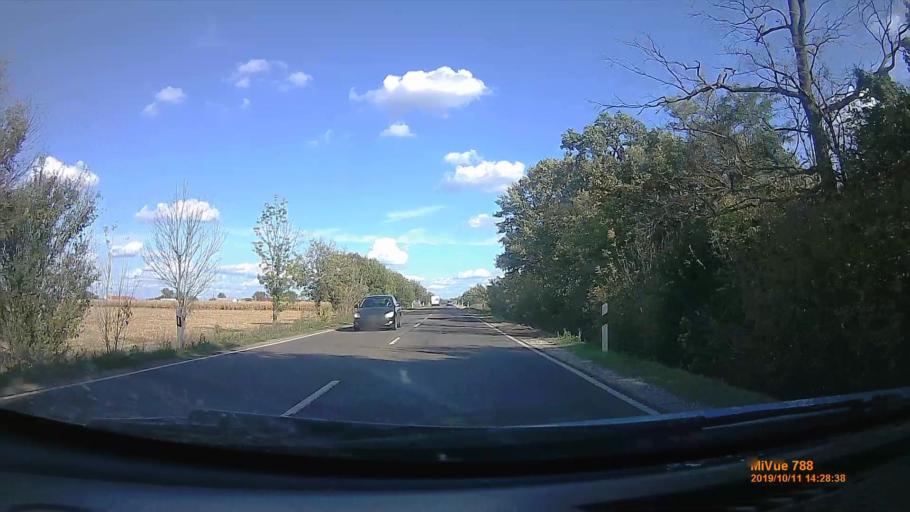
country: HU
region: Hajdu-Bihar
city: Balmazujvaros
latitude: 47.5574
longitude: 21.3703
